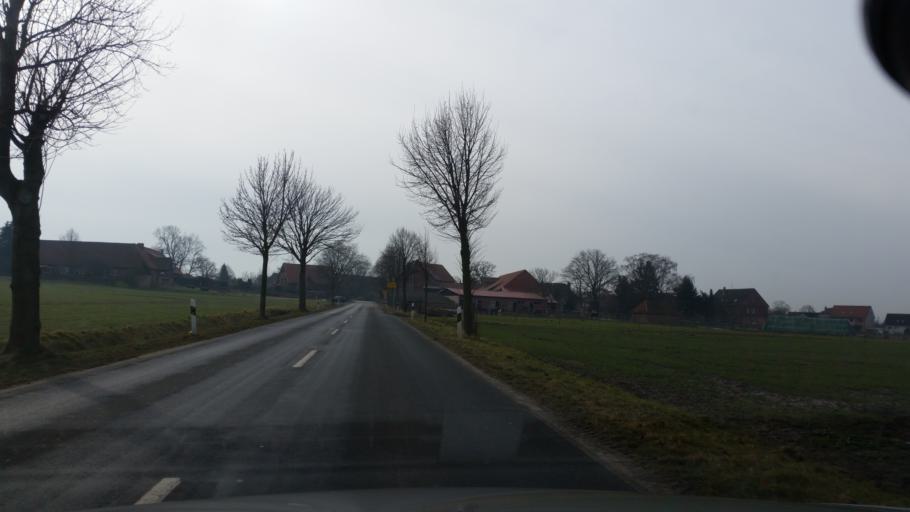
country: DE
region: Lower Saxony
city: Seelze
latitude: 52.3763
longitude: 9.5931
